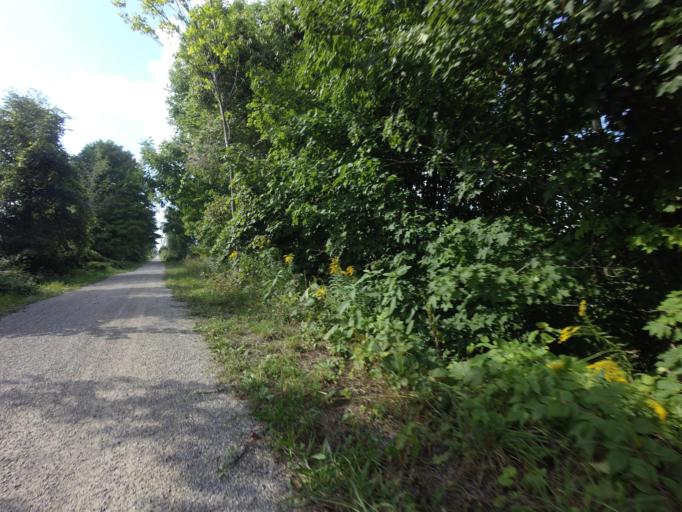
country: CA
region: Ontario
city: Goderich
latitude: 43.7512
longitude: -81.5046
